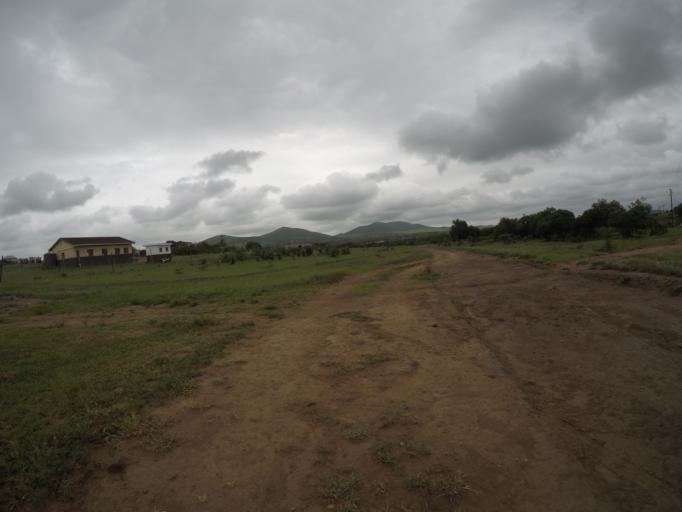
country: ZA
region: KwaZulu-Natal
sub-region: uThungulu District Municipality
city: Empangeni
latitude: -28.6089
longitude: 31.8648
